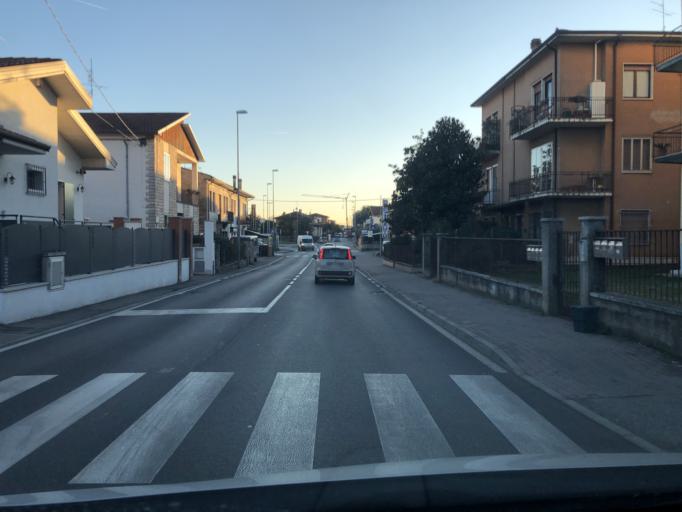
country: IT
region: Veneto
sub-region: Provincia di Verona
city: Villafranca di Verona
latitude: 45.3585
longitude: 10.8439
